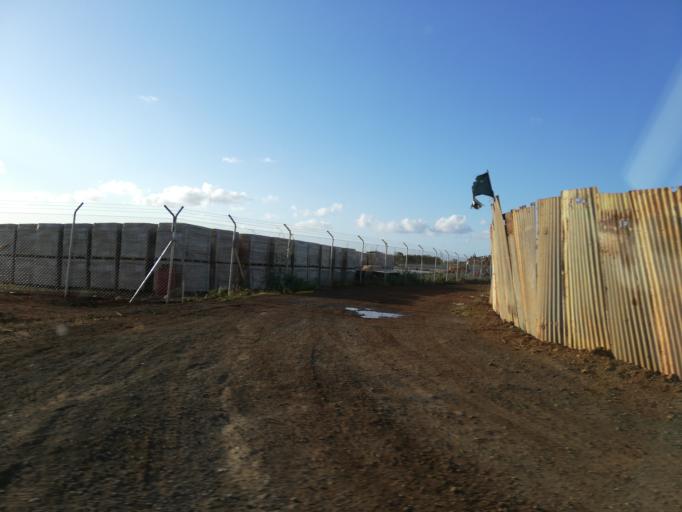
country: MU
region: Pamplemousses
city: Morcellemont Saint Andre
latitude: -20.0800
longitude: 57.5353
